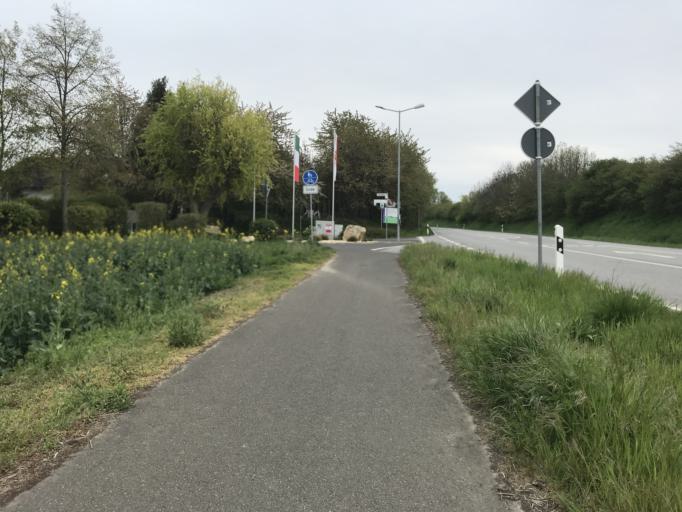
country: DE
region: Rheinland-Pfalz
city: Appenheim
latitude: 49.9344
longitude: 8.0300
